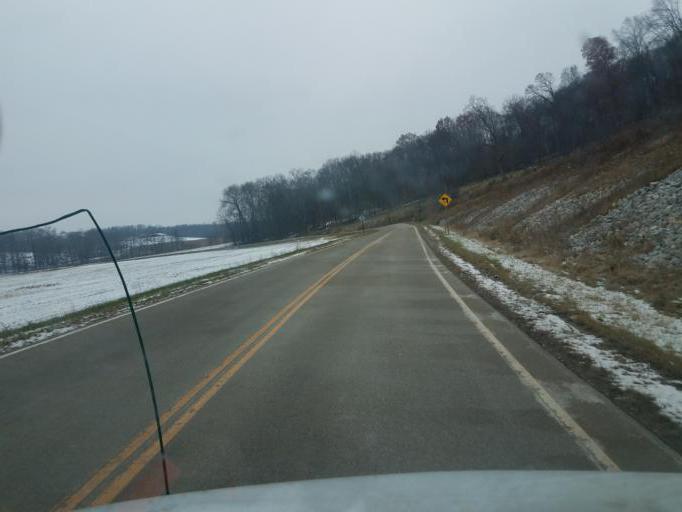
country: US
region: Ohio
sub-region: Sandusky County
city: Bellville
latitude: 40.6297
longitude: -82.4074
